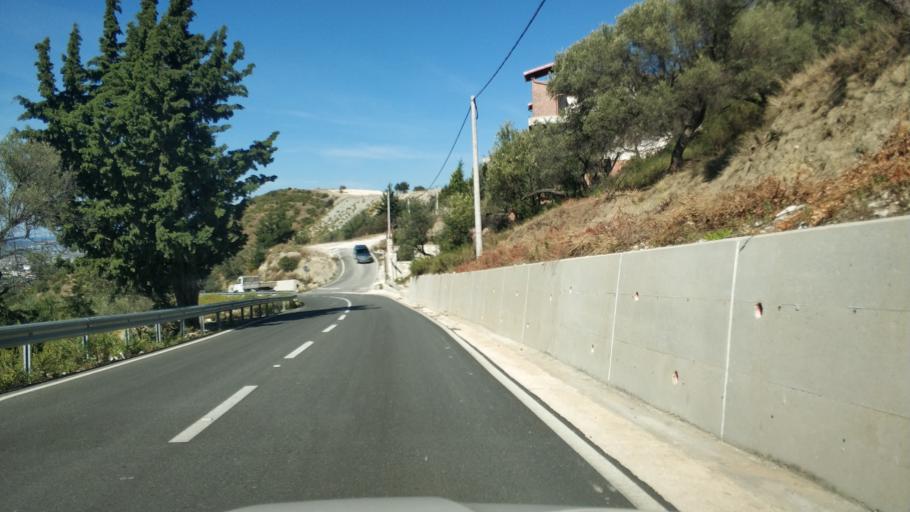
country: AL
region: Vlore
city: Vlore
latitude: 40.4551
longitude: 19.5150
